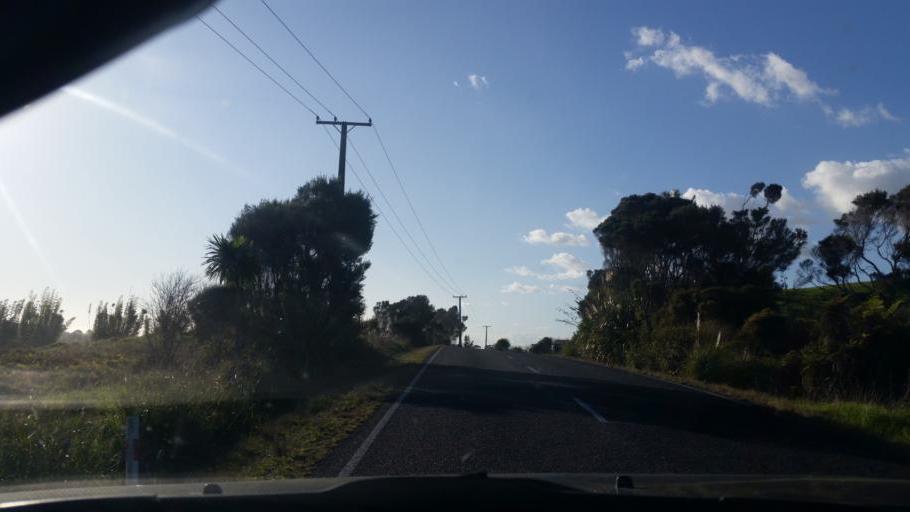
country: NZ
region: Northland
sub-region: Kaipara District
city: Dargaville
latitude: -36.1180
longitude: 173.9593
